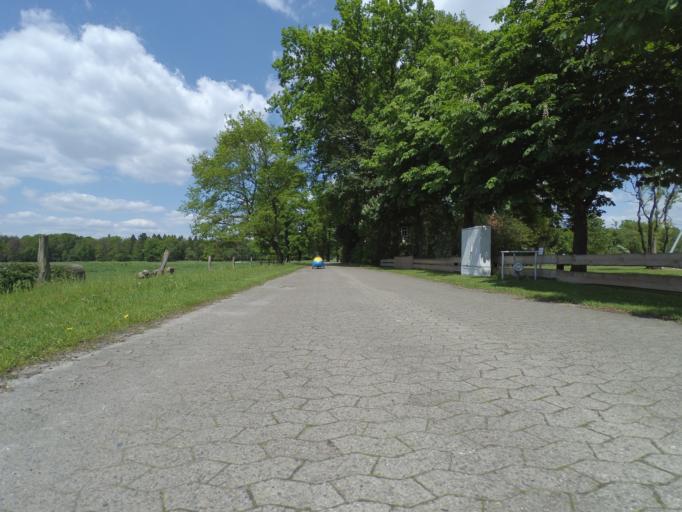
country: DE
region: Lower Saxony
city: Ummern
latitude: 52.6043
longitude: 10.4562
